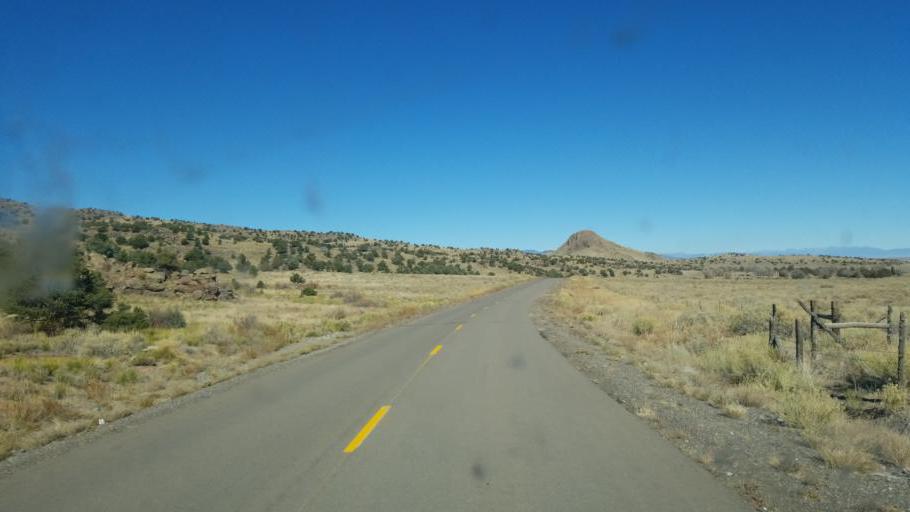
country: US
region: Colorado
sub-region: Rio Grande County
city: Del Norte
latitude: 37.6503
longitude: -106.3648
